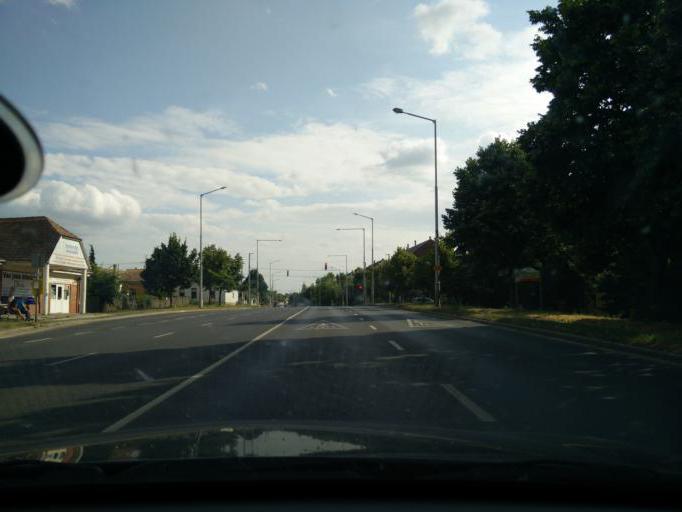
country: HU
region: Komarom-Esztergom
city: Tata
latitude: 47.6448
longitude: 18.3104
